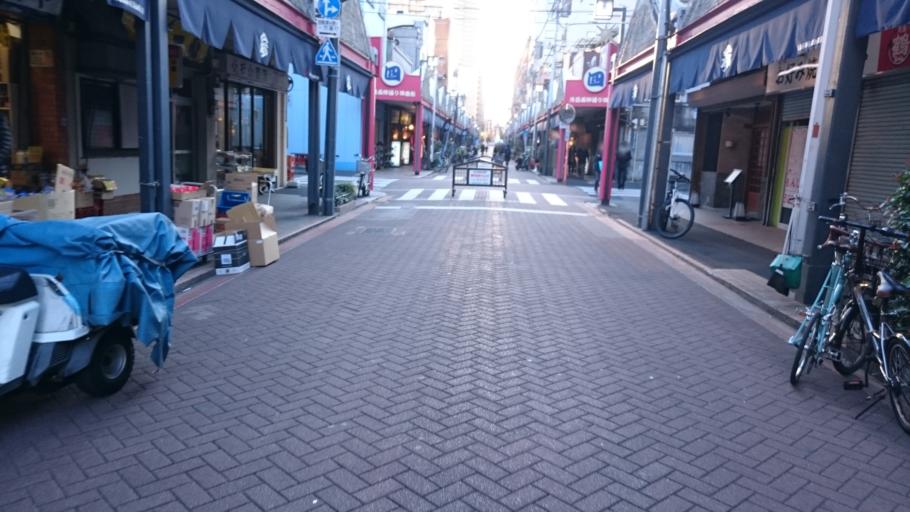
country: JP
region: Tokyo
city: Tokyo
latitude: 35.6632
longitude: 139.7809
